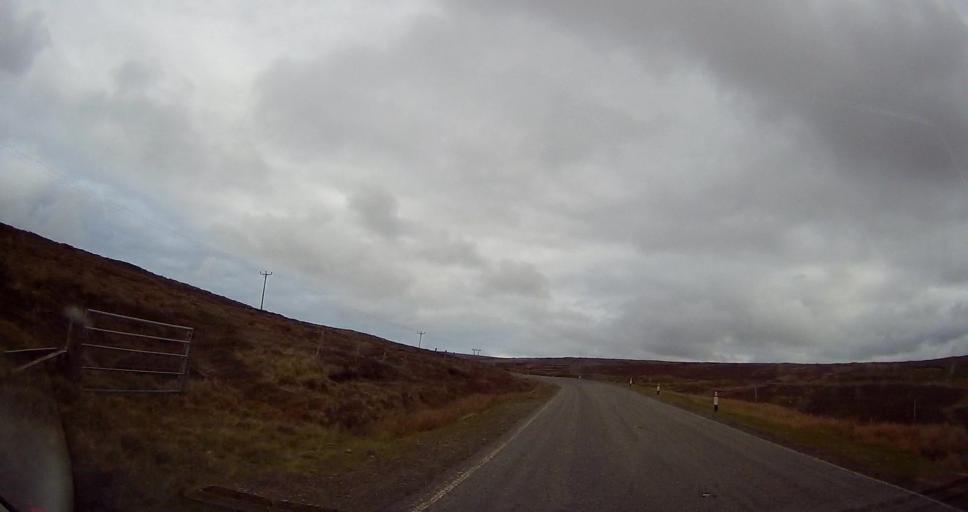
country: GB
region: Scotland
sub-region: Shetland Islands
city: Shetland
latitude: 60.6149
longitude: -1.0745
